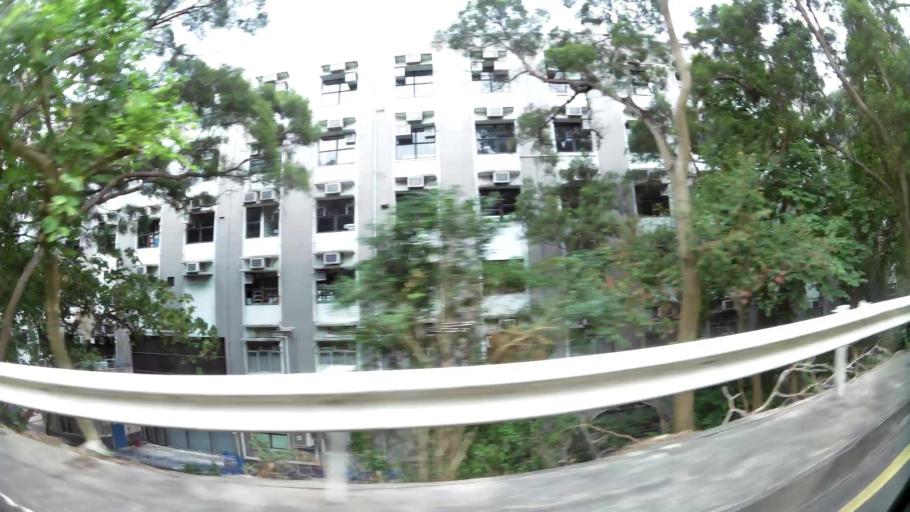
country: HK
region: Sha Tin
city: Sha Tin
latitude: 22.3927
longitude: 114.1974
